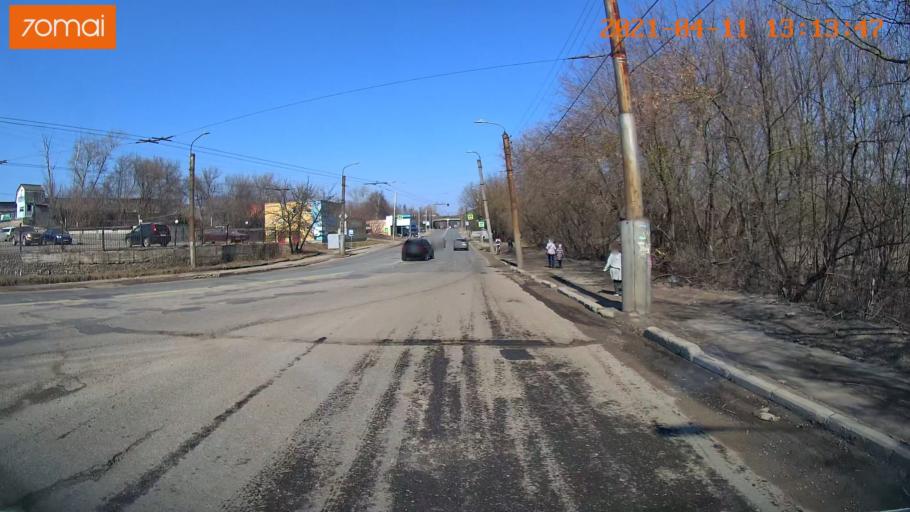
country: RU
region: Ivanovo
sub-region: Gorod Ivanovo
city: Ivanovo
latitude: 57.0109
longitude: 41.0003
